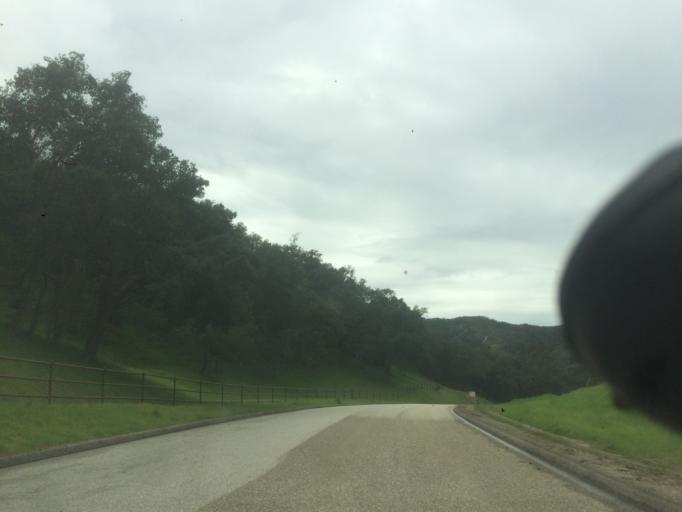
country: US
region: California
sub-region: San Luis Obispo County
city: Nipomo
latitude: 35.2074
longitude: -120.3711
